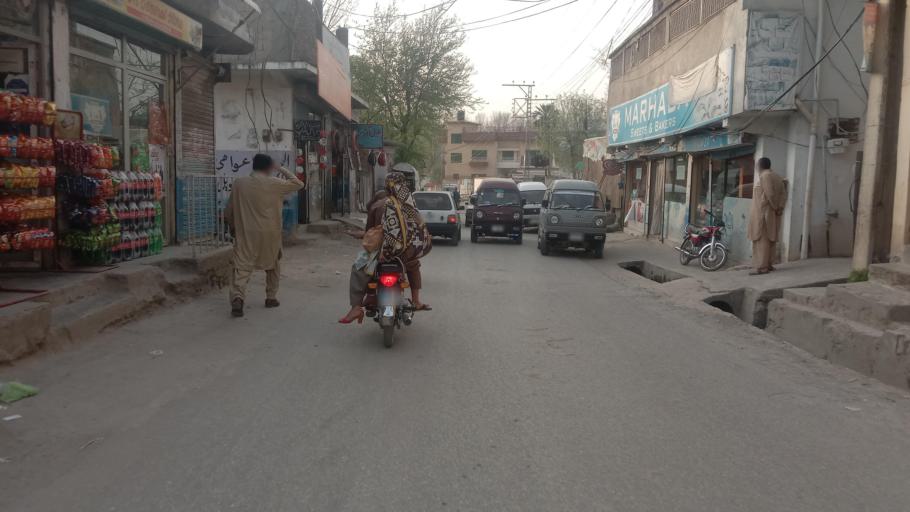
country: PK
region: Khyber Pakhtunkhwa
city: Abbottabad
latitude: 34.1745
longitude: 73.2436
